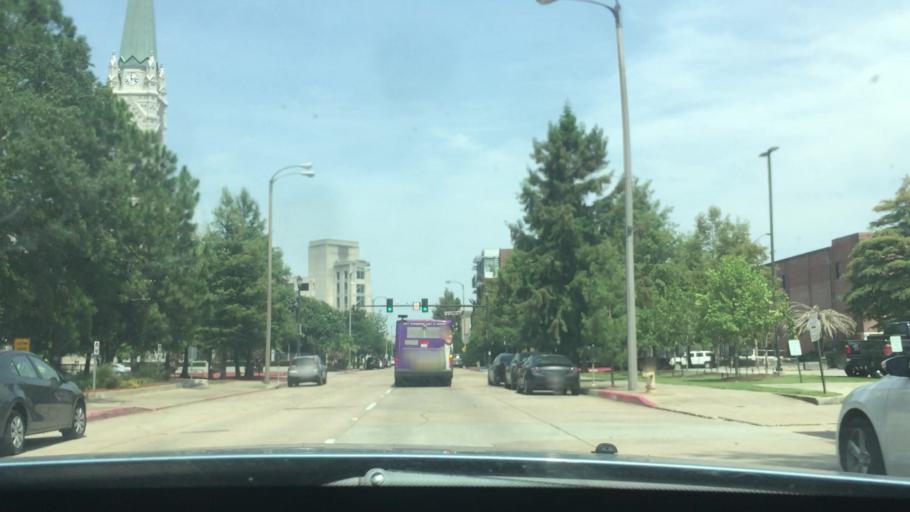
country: US
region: Louisiana
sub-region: West Baton Rouge Parish
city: Port Allen
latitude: 30.4515
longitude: -91.1882
